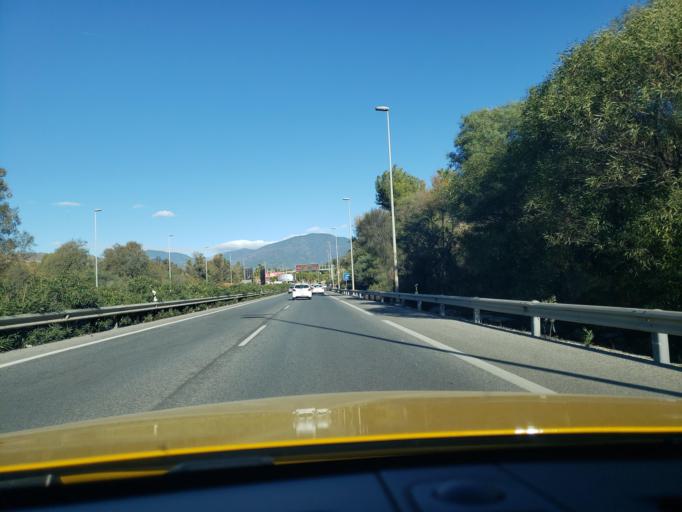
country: ES
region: Andalusia
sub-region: Provincia de Malaga
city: Marbella
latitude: 36.5066
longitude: -4.9479
